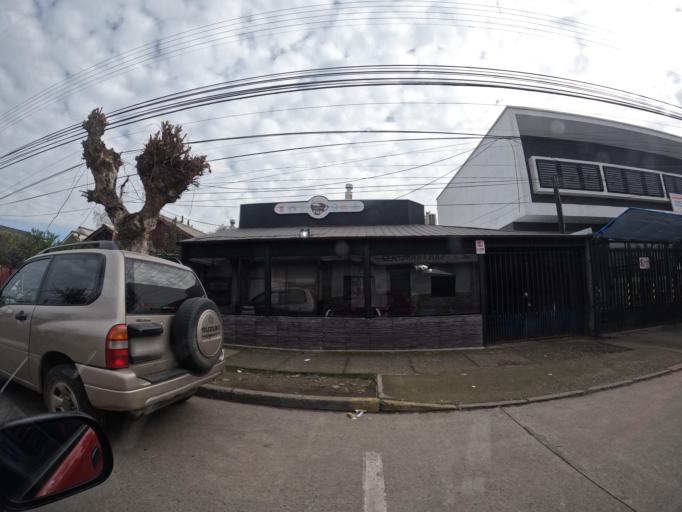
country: CL
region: Maule
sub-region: Provincia de Linares
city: Linares
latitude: -35.8437
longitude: -71.6013
